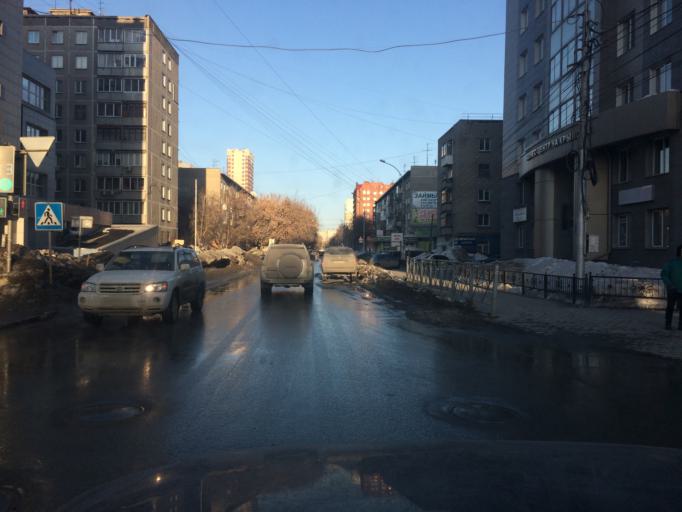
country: RU
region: Novosibirsk
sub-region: Novosibirskiy Rayon
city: Novosibirsk
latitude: 55.0413
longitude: 82.9296
